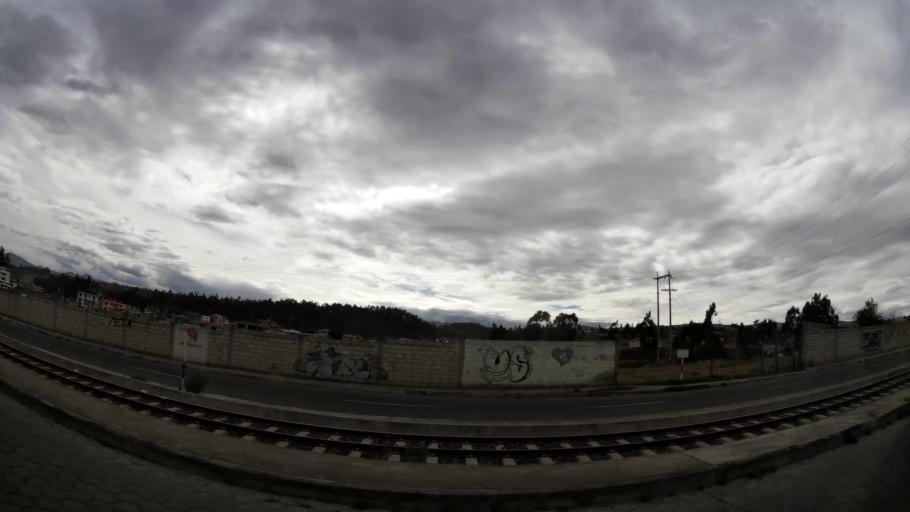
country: EC
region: Cotopaxi
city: Latacunga
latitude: -0.9433
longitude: -78.6181
